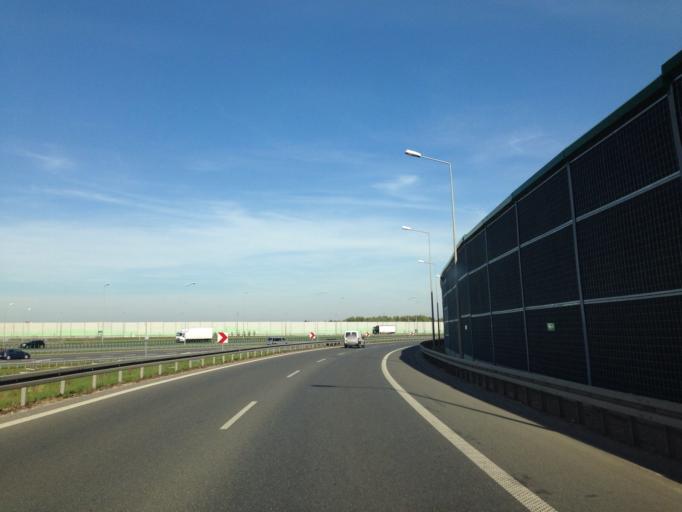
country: PL
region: Masovian Voivodeship
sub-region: Powiat warszawski zachodni
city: Ozarow Mazowiecki
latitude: 52.1875
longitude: 20.7799
